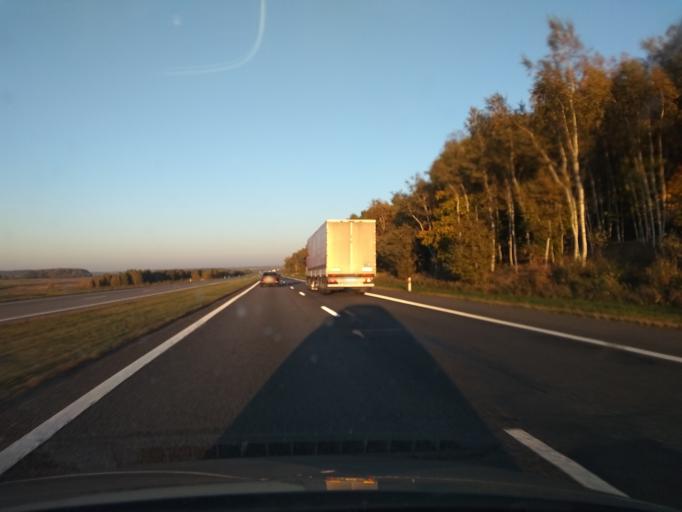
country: BY
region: Minsk
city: Snow
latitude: 53.2439
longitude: 26.2011
